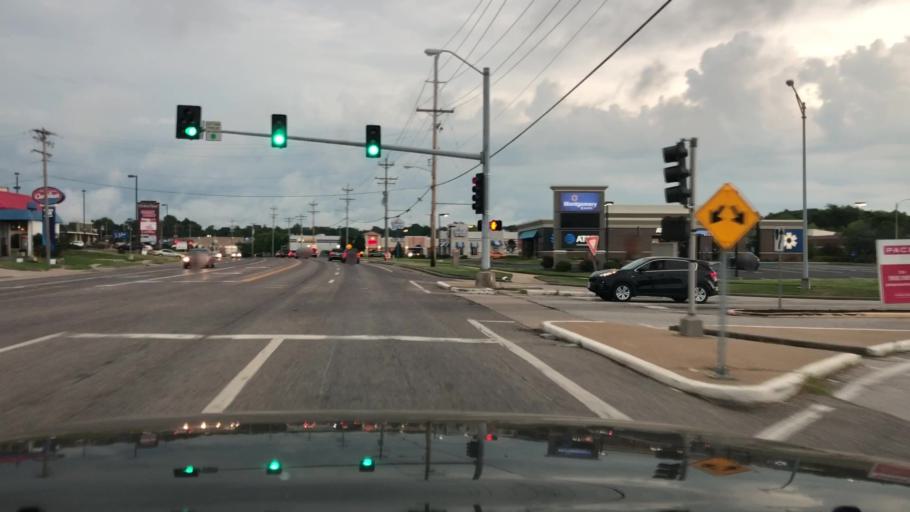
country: US
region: Missouri
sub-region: Saint Louis County
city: Bridgeton
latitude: 38.7487
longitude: -90.4237
